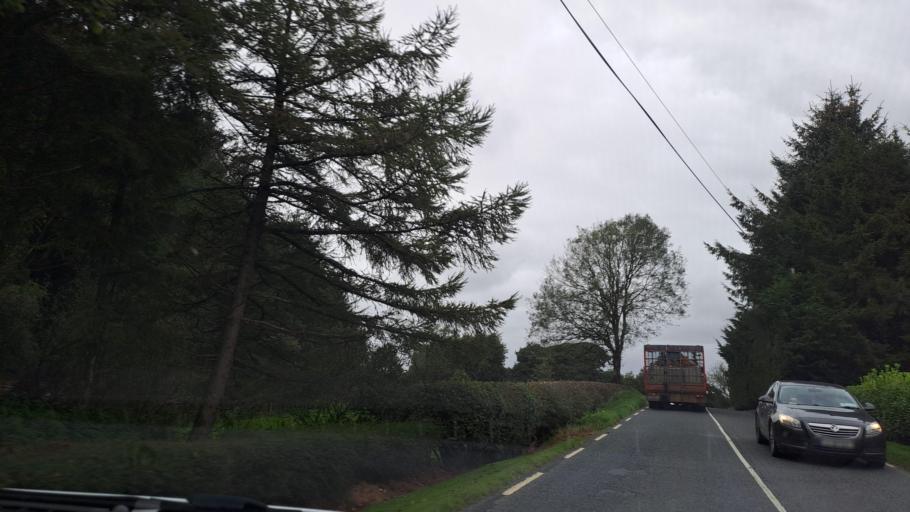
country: IE
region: Ulster
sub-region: County Monaghan
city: Castleblayney
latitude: 54.0867
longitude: -6.8284
